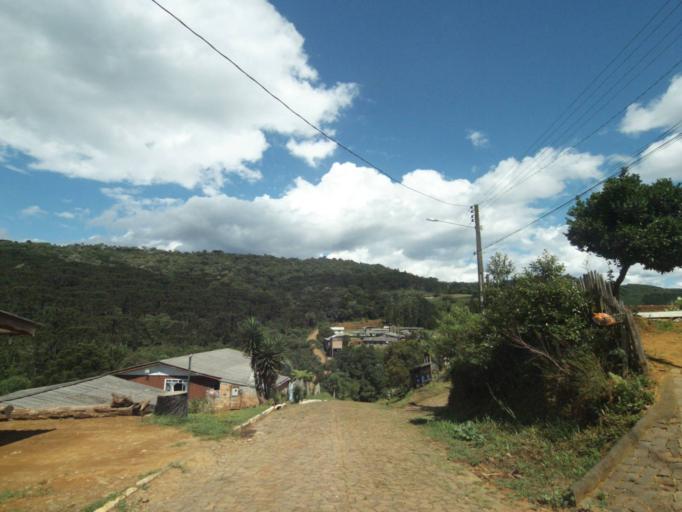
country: BR
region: Parana
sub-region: Uniao Da Vitoria
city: Uniao da Vitoria
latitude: -26.1713
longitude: -51.5501
